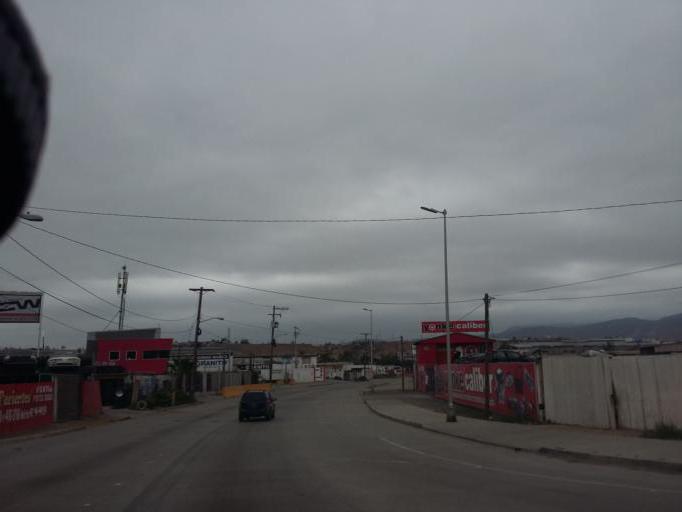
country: MX
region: Baja California
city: Tijuana
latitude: 32.5165
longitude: -116.9258
